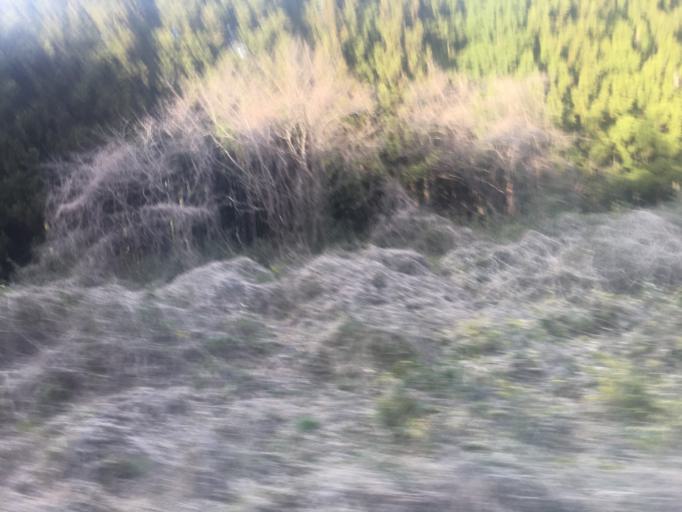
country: JP
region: Fukushima
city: Iwaki
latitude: 37.2076
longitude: 140.7450
